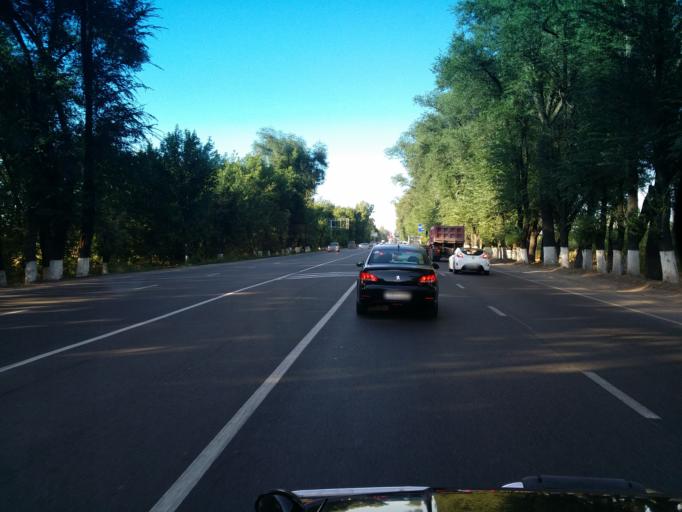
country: KZ
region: Almaty Oblysy
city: Pervomayskiy
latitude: 43.3147
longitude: 77.0212
